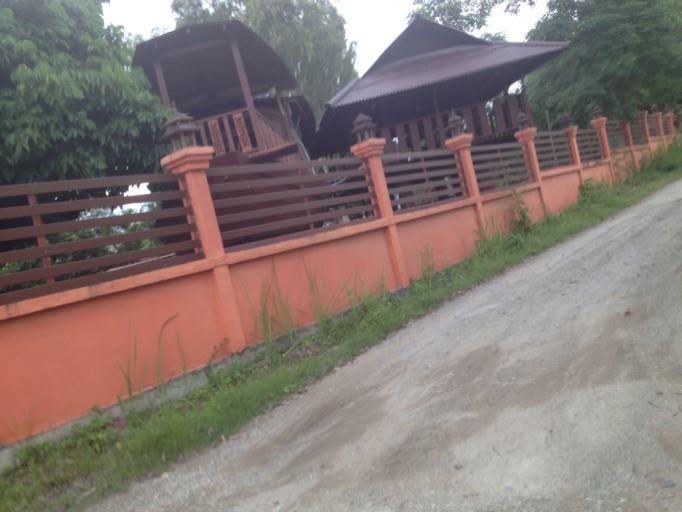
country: TH
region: Chiang Mai
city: Hang Dong
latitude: 18.6902
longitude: 98.8858
